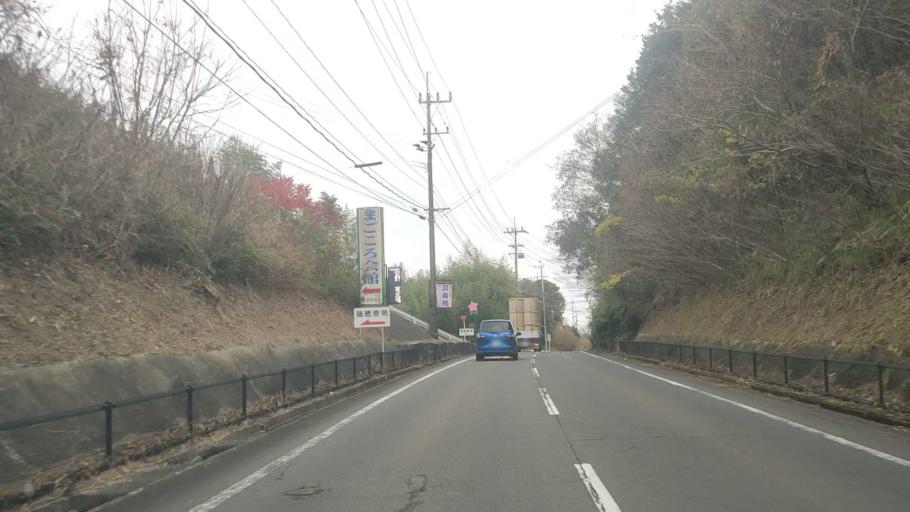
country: JP
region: Nagasaki
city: Shimabara
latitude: 32.8519
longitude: 130.2410
